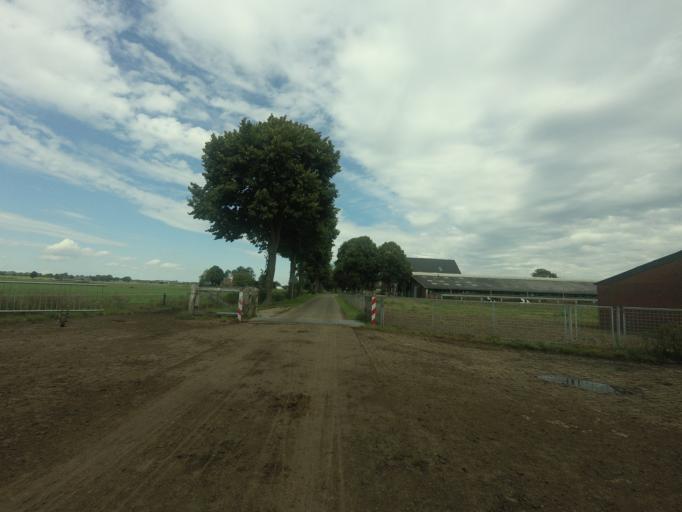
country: NL
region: Overijssel
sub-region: Gemeente Raalte
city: Raalte
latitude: 52.4567
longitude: 6.3598
